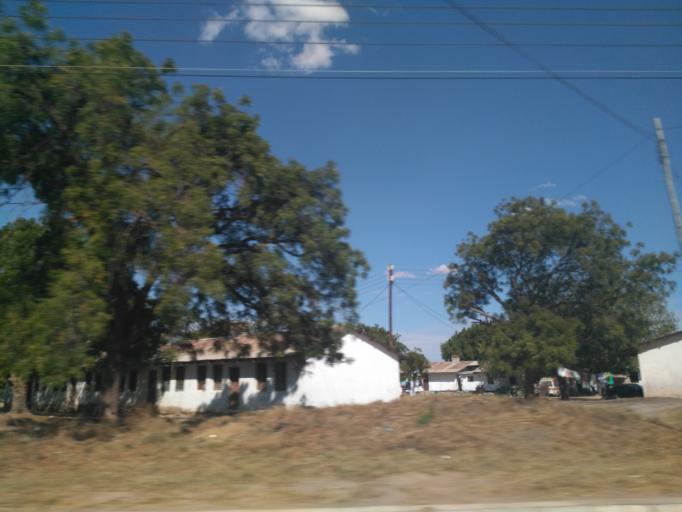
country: TZ
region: Dodoma
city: Dodoma
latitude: -6.1866
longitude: 35.7417
